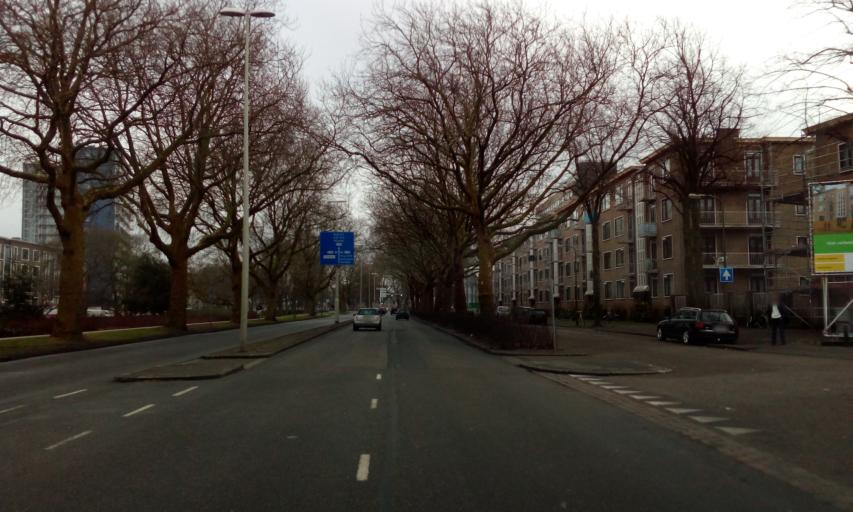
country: NL
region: South Holland
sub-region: Gemeente Den Haag
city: The Hague
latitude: 52.0527
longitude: 4.2975
